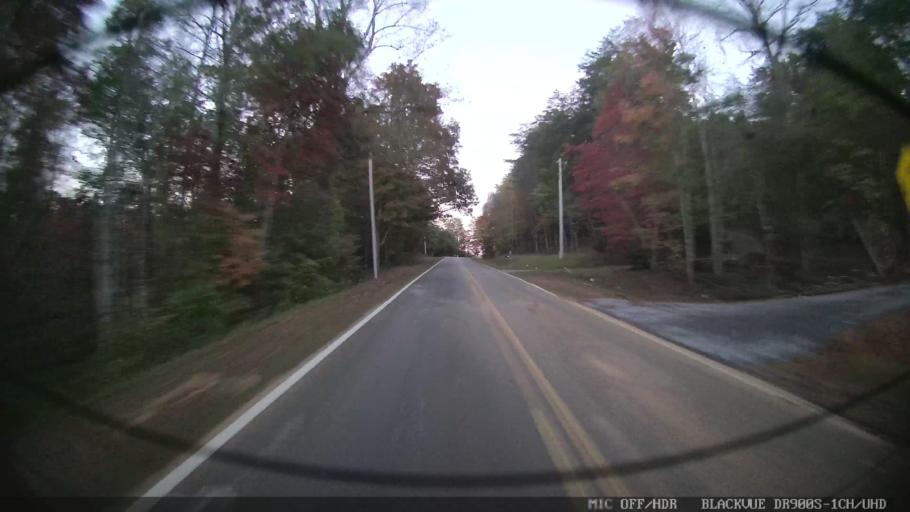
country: US
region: North Carolina
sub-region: Clay County
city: Hayesville
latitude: 34.9645
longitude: -83.8870
